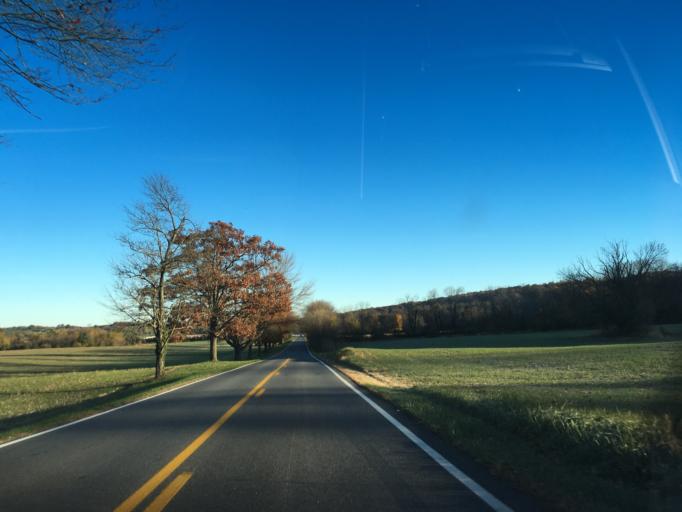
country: US
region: Maryland
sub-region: Baltimore County
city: Owings Mills
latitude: 39.4701
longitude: -76.7640
